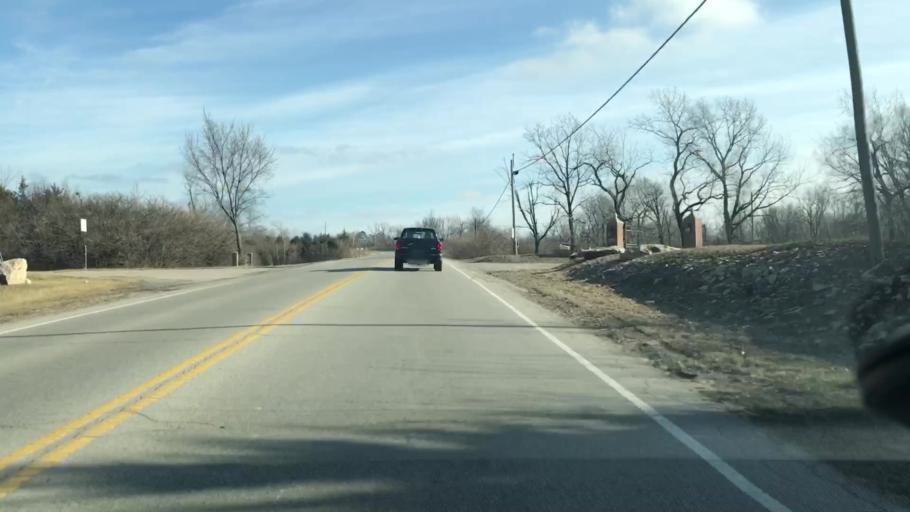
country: US
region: Ohio
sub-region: Greene County
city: Fairborn
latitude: 39.8144
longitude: -83.9958
